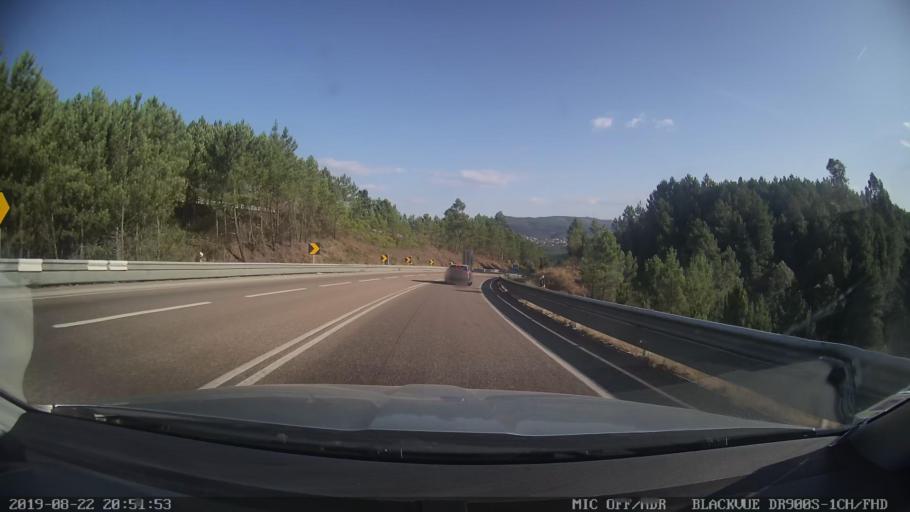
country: PT
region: Castelo Branco
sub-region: Proenca-A-Nova
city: Proenca-a-Nova
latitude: 39.7638
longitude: -7.9668
